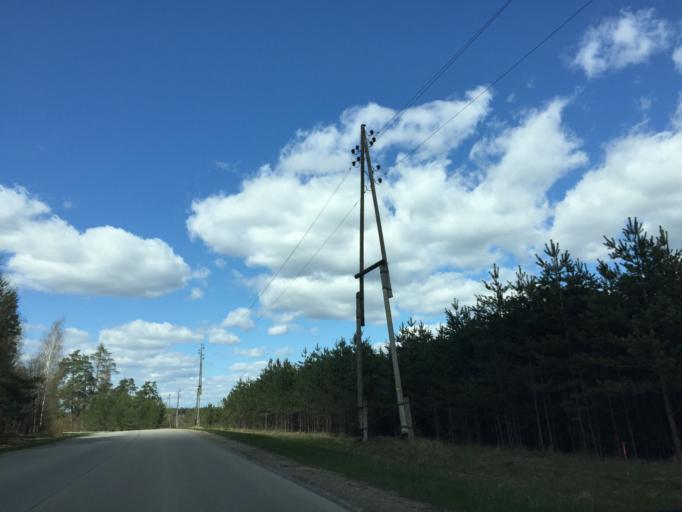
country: LV
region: Vilanu
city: Vilani
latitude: 56.5624
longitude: 27.0542
